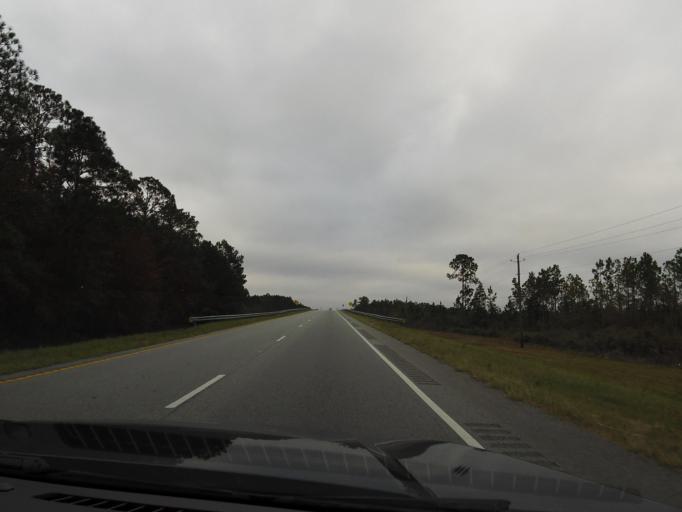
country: US
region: Georgia
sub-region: Charlton County
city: Folkston
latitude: 30.8702
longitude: -82.0210
